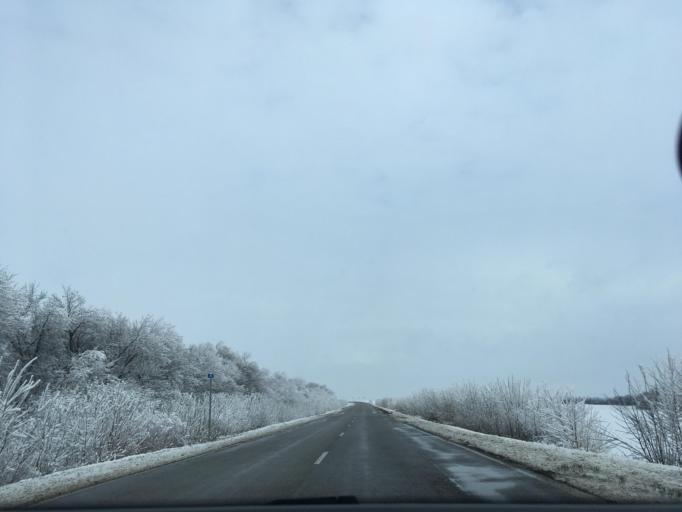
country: UA
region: Luhansk
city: Lozno-Oleksandrivka
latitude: 49.9955
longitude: 39.0348
